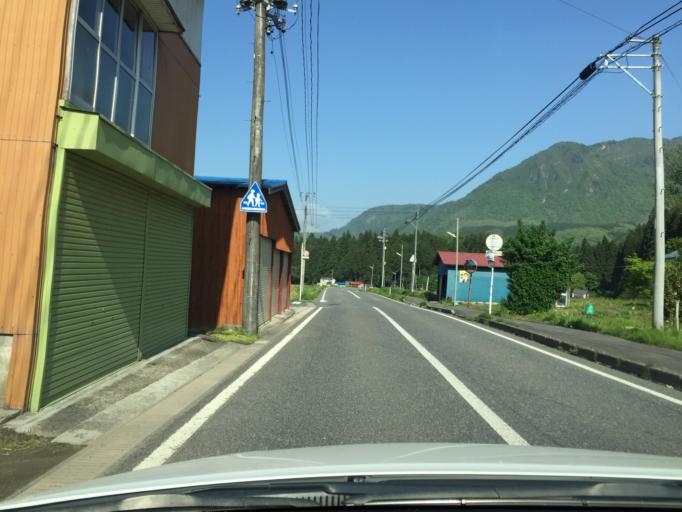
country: JP
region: Niigata
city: Shibata
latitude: 37.7169
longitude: 139.5245
